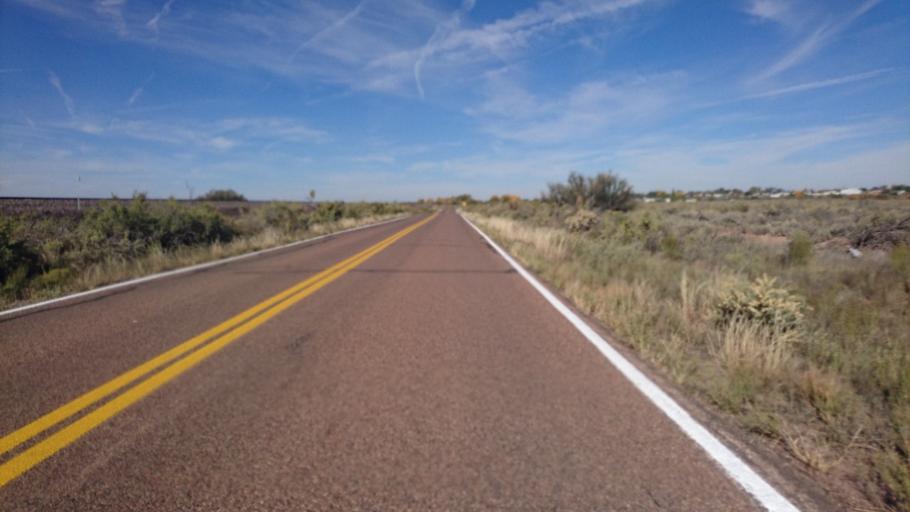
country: US
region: Arizona
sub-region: Navajo County
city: Joseph City
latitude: 34.9465
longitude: -110.3279
